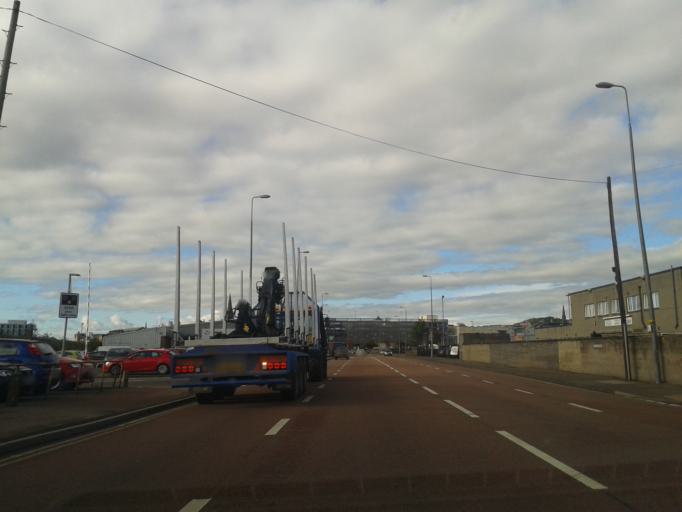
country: GB
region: Scotland
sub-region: Dundee City
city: Dundee
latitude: 56.4642
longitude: -2.9562
